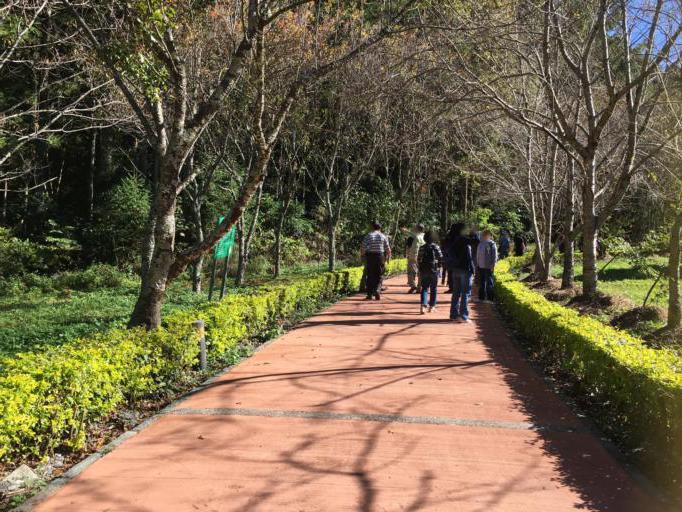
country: TW
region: Taiwan
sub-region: Nantou
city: Puli
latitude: 23.9530
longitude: 121.1795
